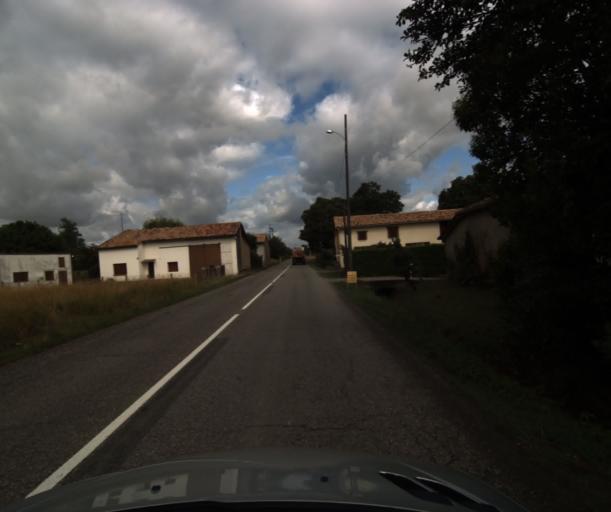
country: FR
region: Midi-Pyrenees
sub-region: Departement du Tarn-et-Garonne
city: Castelsarrasin
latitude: 44.0205
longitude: 1.0690
